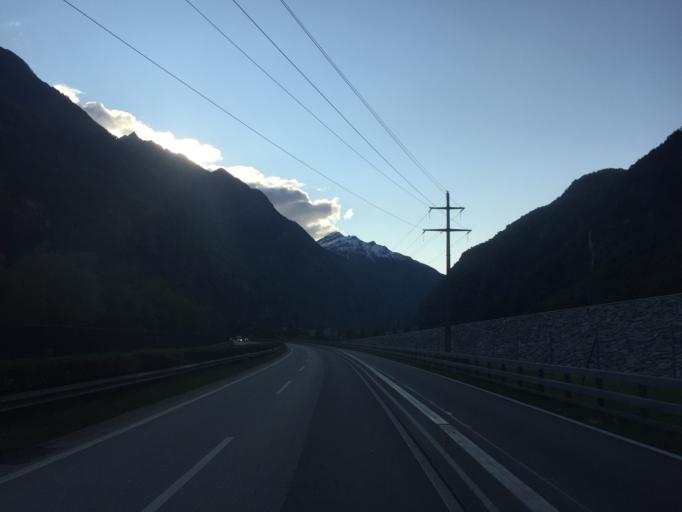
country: CH
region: Ticino
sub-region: Leventina District
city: Bodio
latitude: 46.3727
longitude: 8.9245
